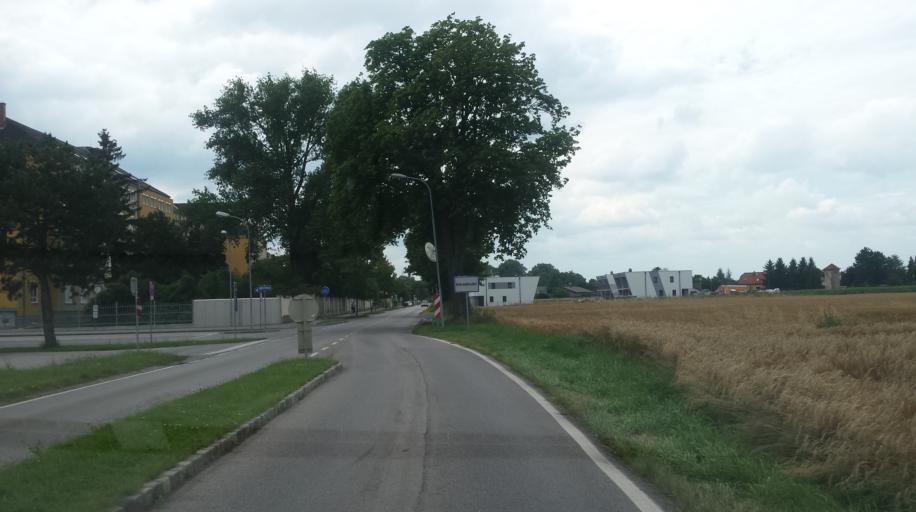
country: AT
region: Lower Austria
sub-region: Politischer Bezirk Baden
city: Ebreichsdorf
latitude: 47.9674
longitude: 16.4307
